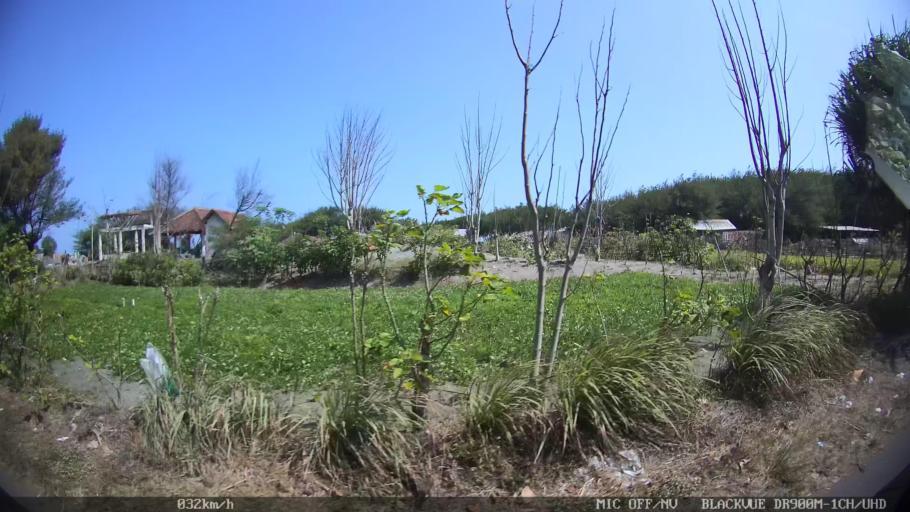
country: ID
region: Daerah Istimewa Yogyakarta
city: Bambanglipuro
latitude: -8.0172
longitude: 110.3088
